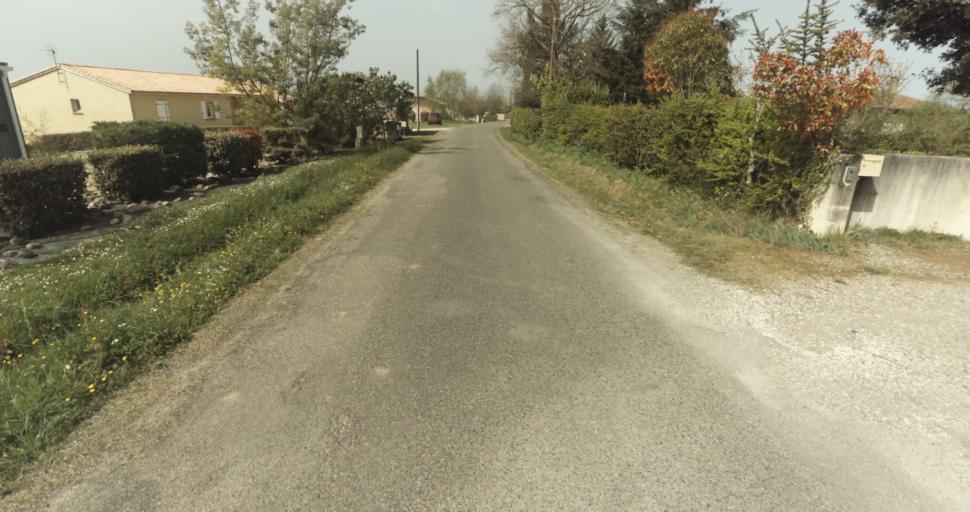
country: FR
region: Midi-Pyrenees
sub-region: Departement du Tarn-et-Garonne
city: Moissac
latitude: 44.1123
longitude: 1.0693
